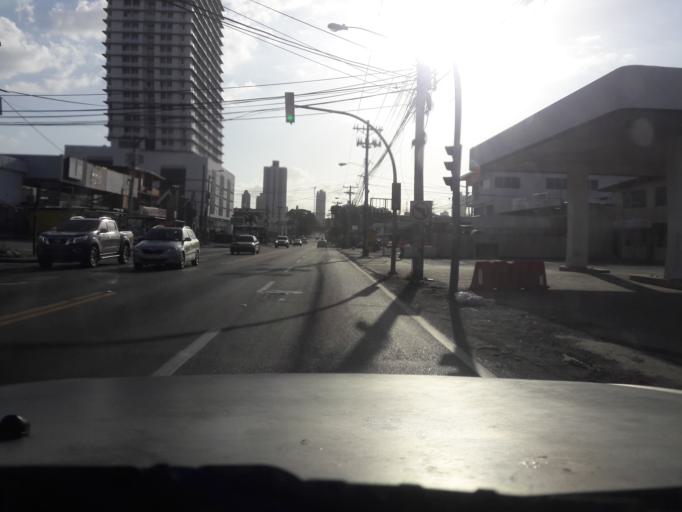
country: PA
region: Panama
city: Panama
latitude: 9.0152
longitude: -79.4983
